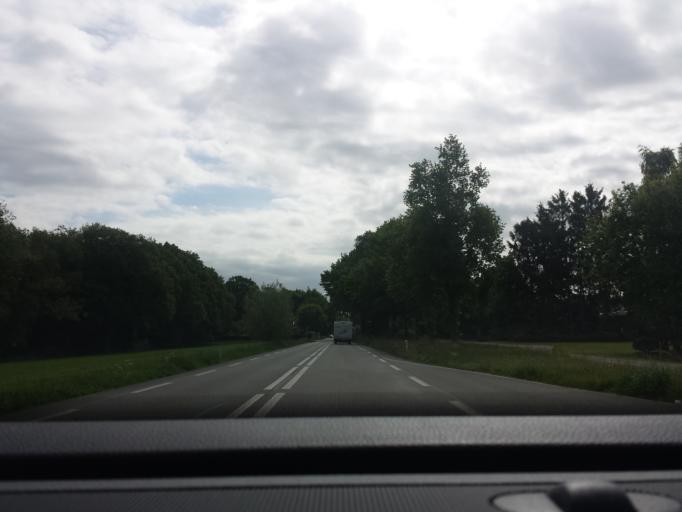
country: NL
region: Gelderland
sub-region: Gemeente Lochem
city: Barchem
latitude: 52.0979
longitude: 6.3846
